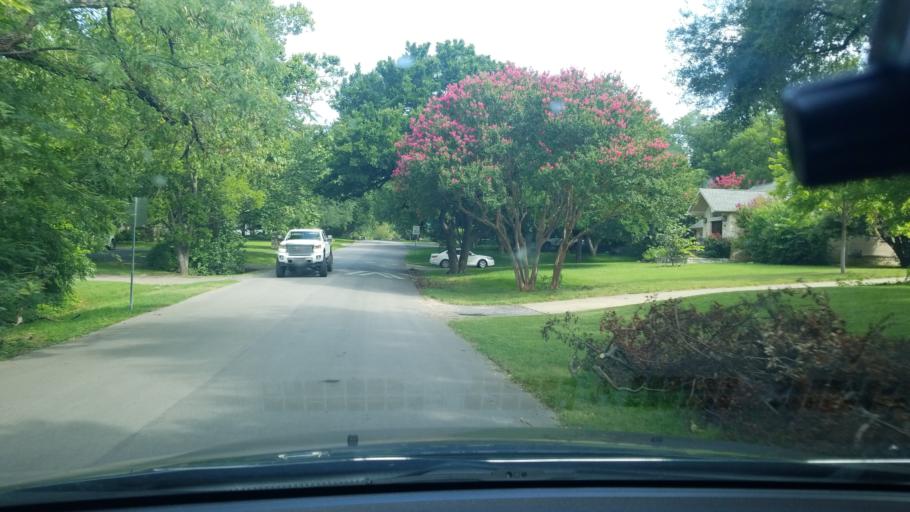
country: US
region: Texas
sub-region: Dallas County
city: Highland Park
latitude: 32.8232
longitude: -96.7014
